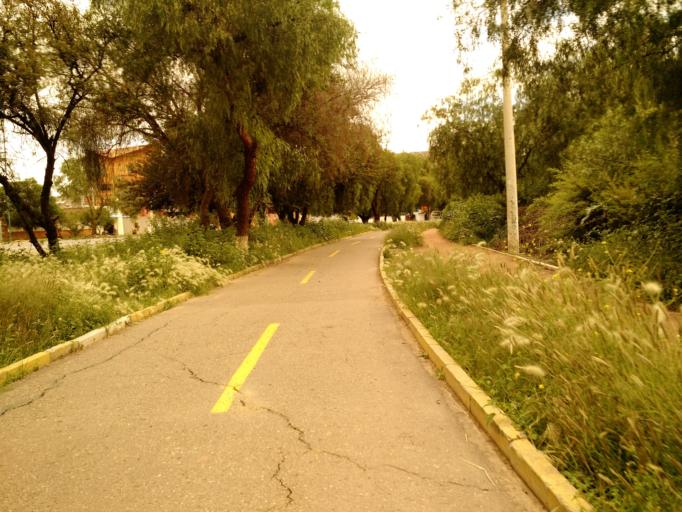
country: BO
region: Cochabamba
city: Cochabamba
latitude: -17.4164
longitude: -66.1266
